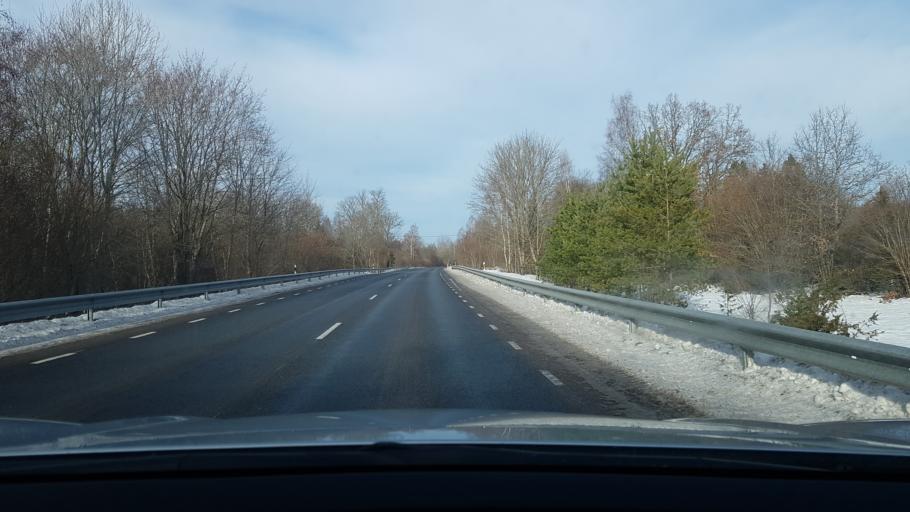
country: EE
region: Saare
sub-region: Kuressaare linn
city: Kuressaare
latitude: 58.3012
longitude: 22.5393
